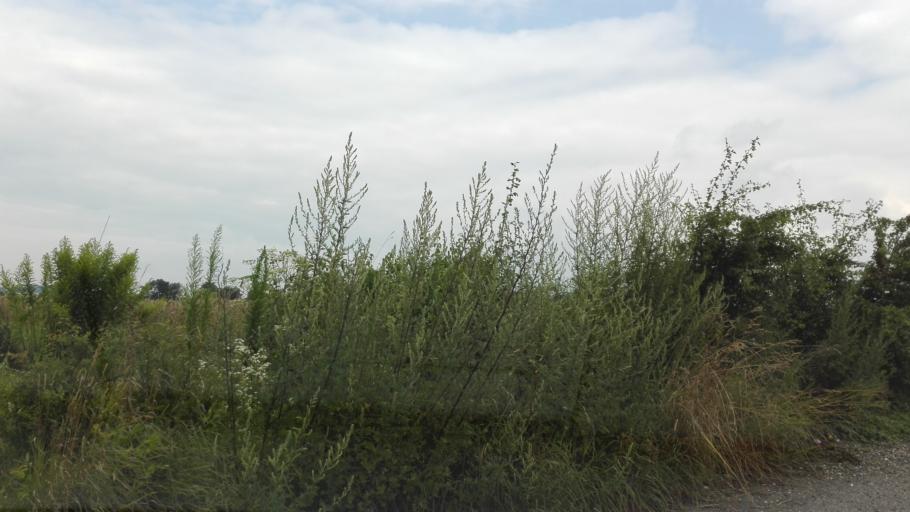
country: AT
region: Upper Austria
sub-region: Politischer Bezirk Linz-Land
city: Traun
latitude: 48.2510
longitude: 14.2348
